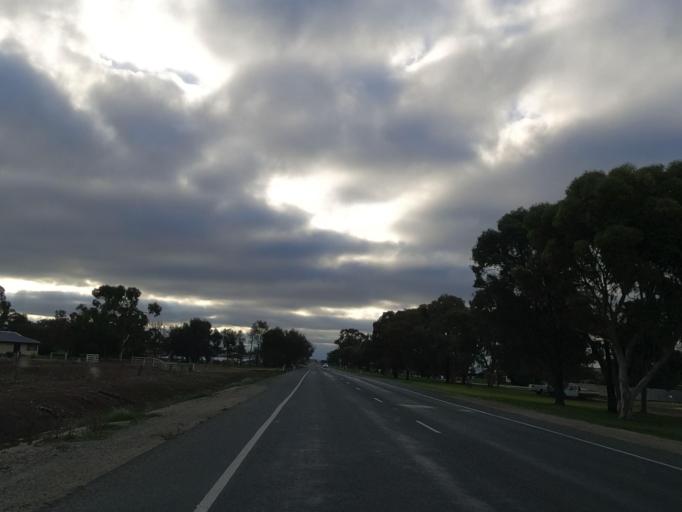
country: AU
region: Victoria
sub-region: Swan Hill
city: Swan Hill
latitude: -35.7438
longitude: 143.9213
